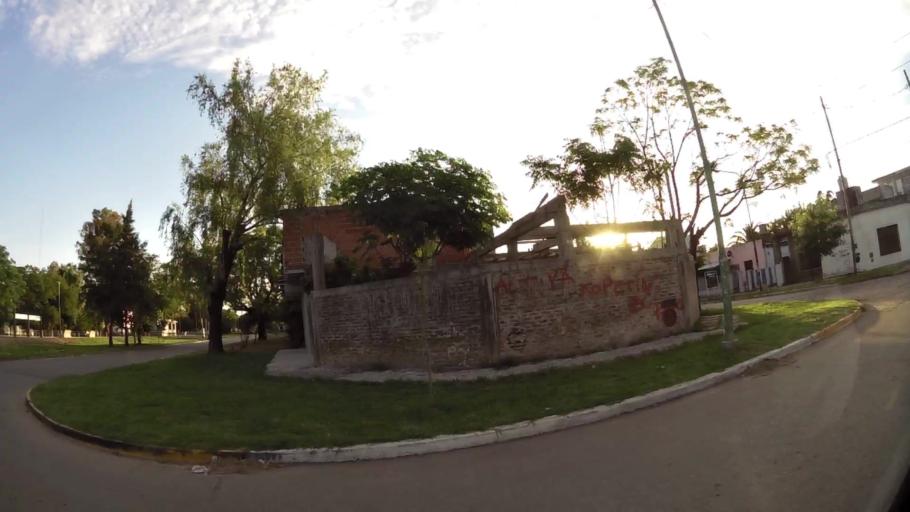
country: AR
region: Buenos Aires
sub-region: Partido de Merlo
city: Merlo
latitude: -34.6792
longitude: -58.7600
